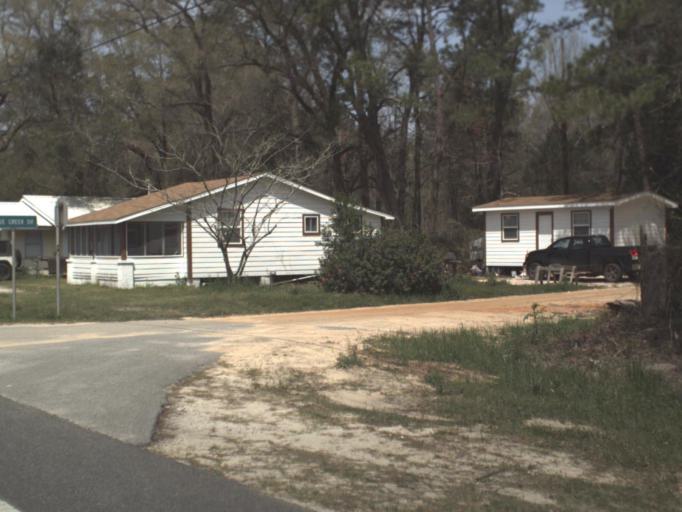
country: US
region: Florida
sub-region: Walton County
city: DeFuniak Springs
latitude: 30.7287
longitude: -85.9394
